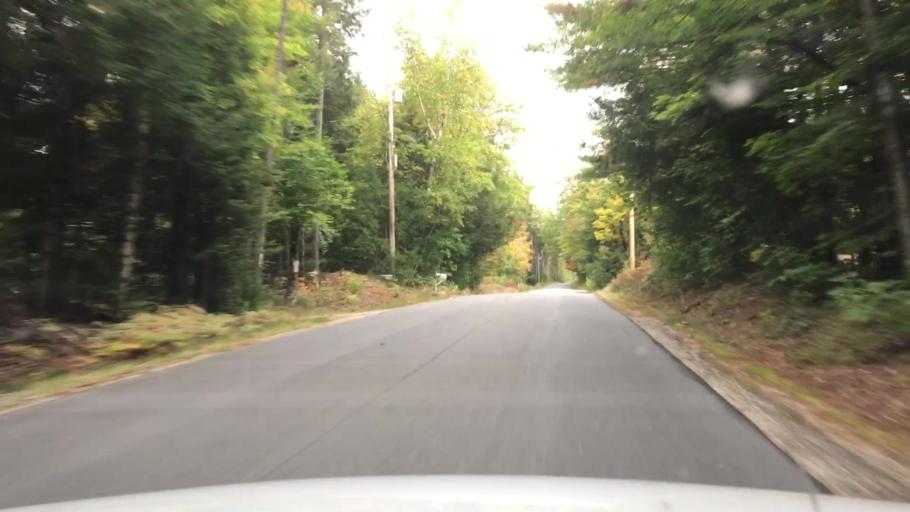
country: US
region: Maine
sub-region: Cumberland County
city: Harrison
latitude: 44.2462
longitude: -70.7201
